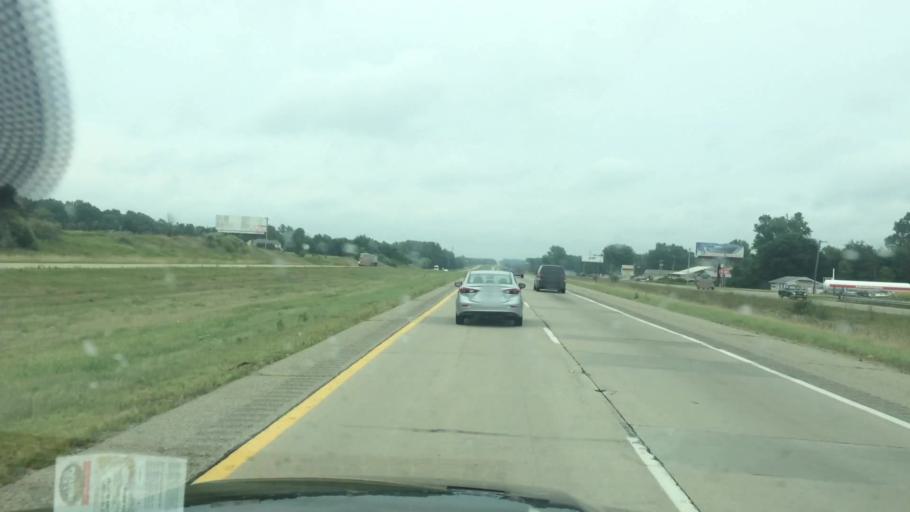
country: US
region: Michigan
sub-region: Eaton County
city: Charlotte
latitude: 42.5924
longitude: -84.7917
